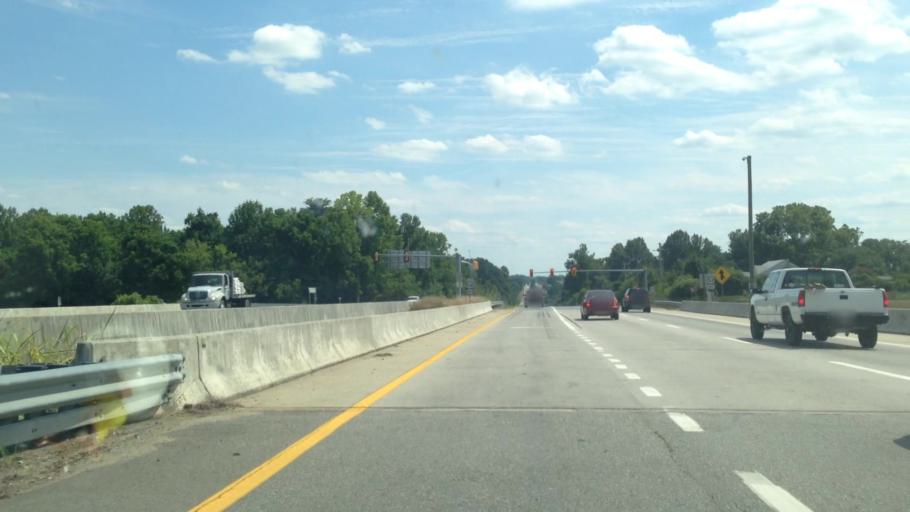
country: US
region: Virginia
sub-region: Henry County
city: Chatmoss
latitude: 36.6231
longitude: -79.8600
